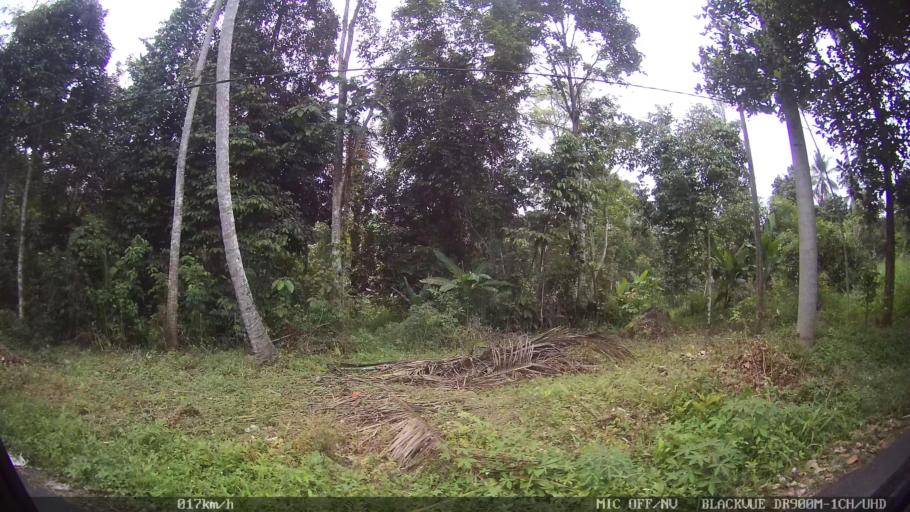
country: ID
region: Lampung
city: Bandarlampung
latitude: -5.4254
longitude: 105.3037
